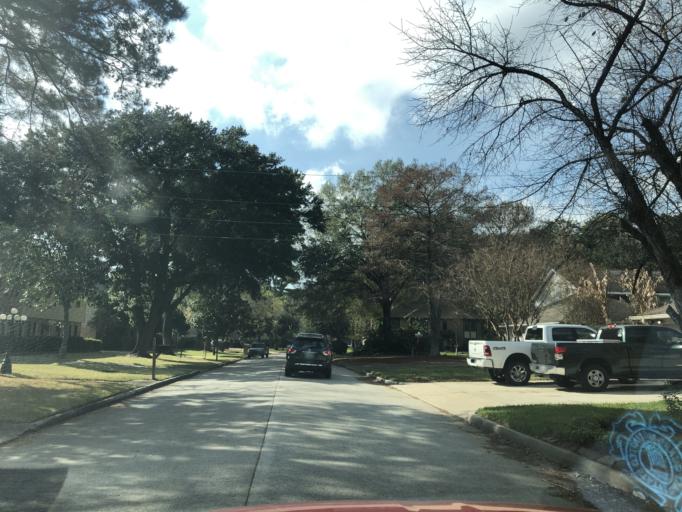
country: US
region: Texas
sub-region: Harris County
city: Tomball
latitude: 30.0258
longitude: -95.5451
